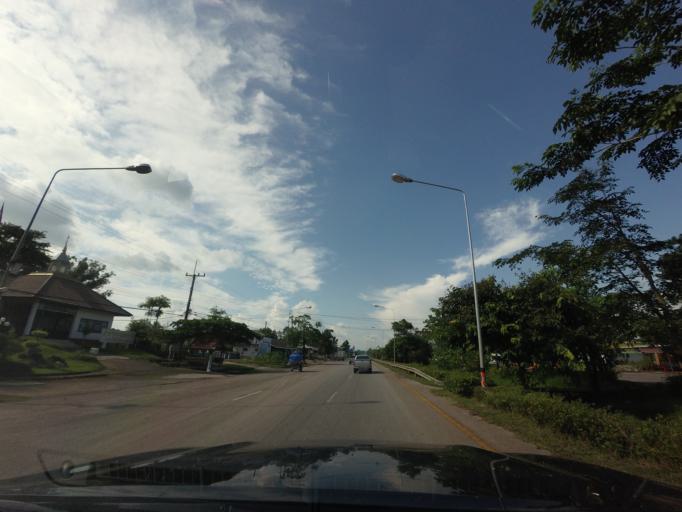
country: TH
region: Nong Khai
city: Sa Khrai
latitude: 17.7620
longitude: 102.7696
